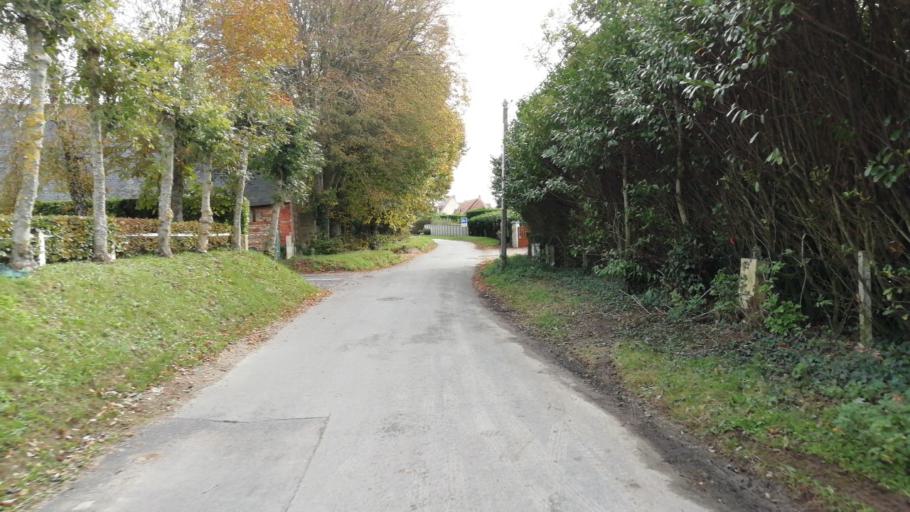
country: FR
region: Haute-Normandie
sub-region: Departement de la Seine-Maritime
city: Octeville-sur-Mer
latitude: 49.5668
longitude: 0.1092
